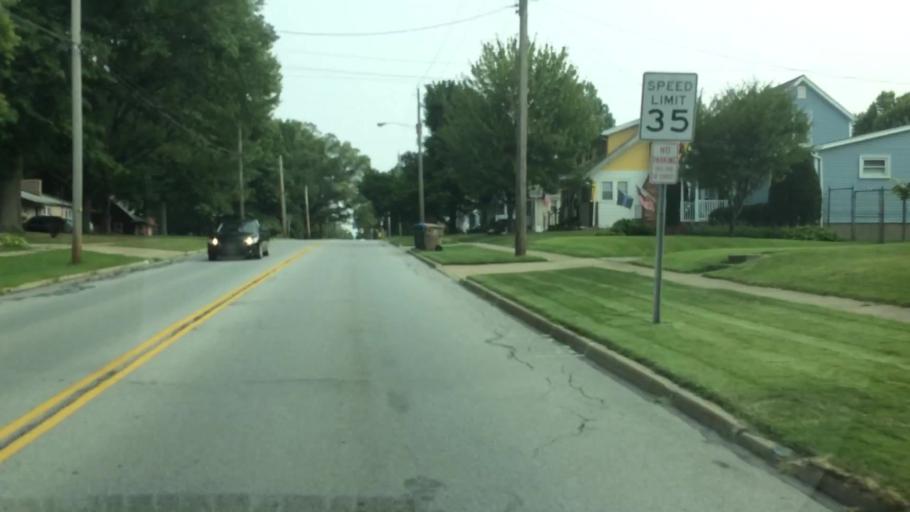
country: US
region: Ohio
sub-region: Summit County
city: Cuyahoga Falls
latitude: 41.1279
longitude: -81.4739
